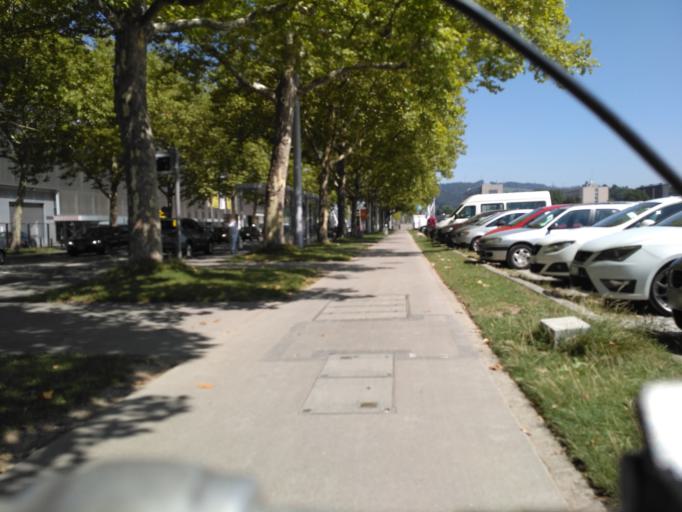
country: CH
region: Bern
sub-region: Bern-Mittelland District
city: Bern
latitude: 46.9618
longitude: 7.4658
